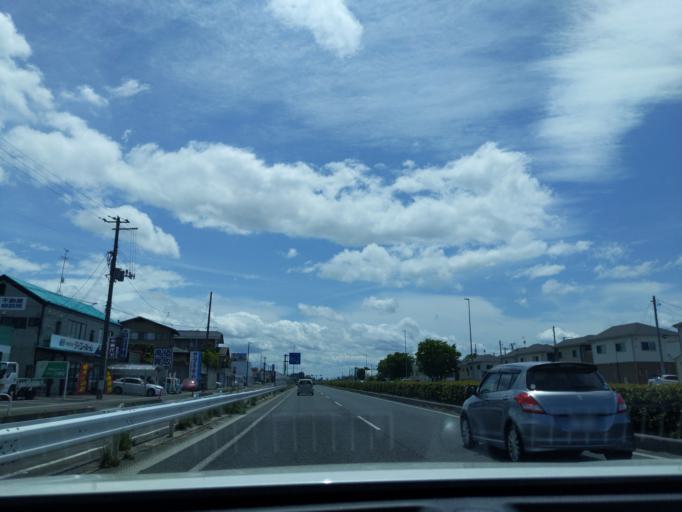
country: JP
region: Fukushima
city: Koriyama
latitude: 37.4041
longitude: 140.3431
